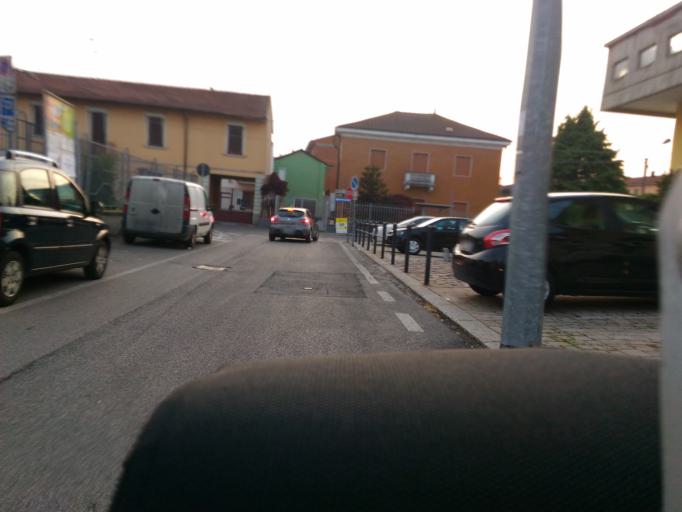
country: IT
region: Lombardy
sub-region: Provincia di Lodi
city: Tavazzano
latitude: 45.3279
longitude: 9.4038
